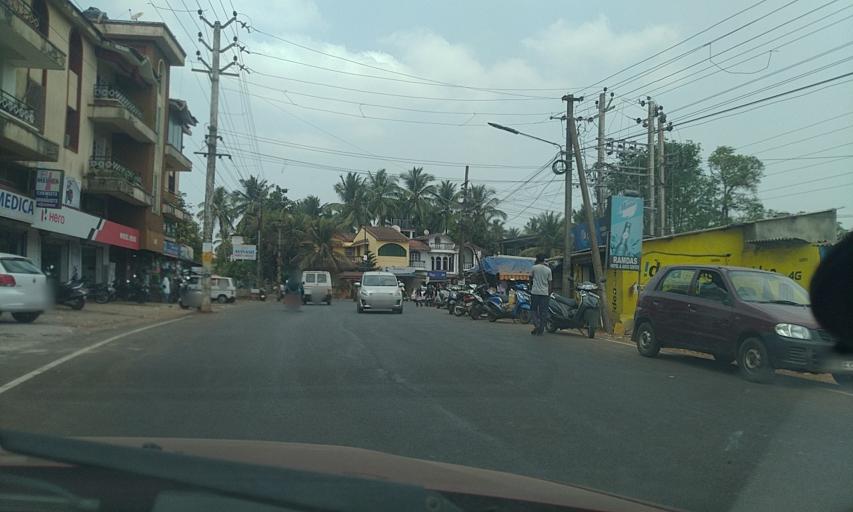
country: IN
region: Goa
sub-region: North Goa
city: Mapuca
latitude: 15.6025
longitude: 73.8051
